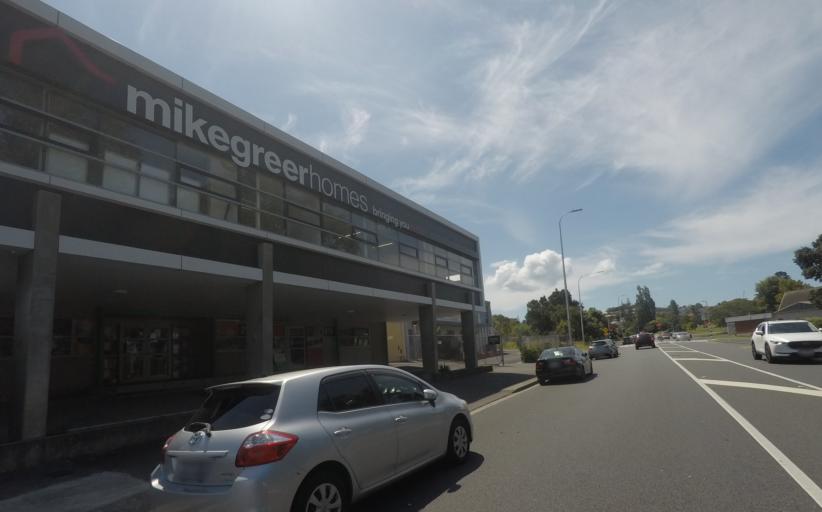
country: NZ
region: Auckland
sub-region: Auckland
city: Tamaki
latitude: -36.8737
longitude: 174.8535
